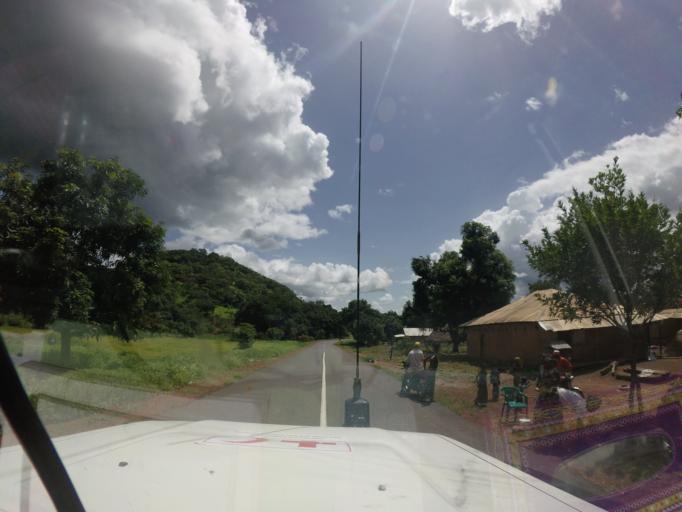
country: SL
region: Northern Province
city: Bindi
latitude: 10.1458
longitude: -11.5895
